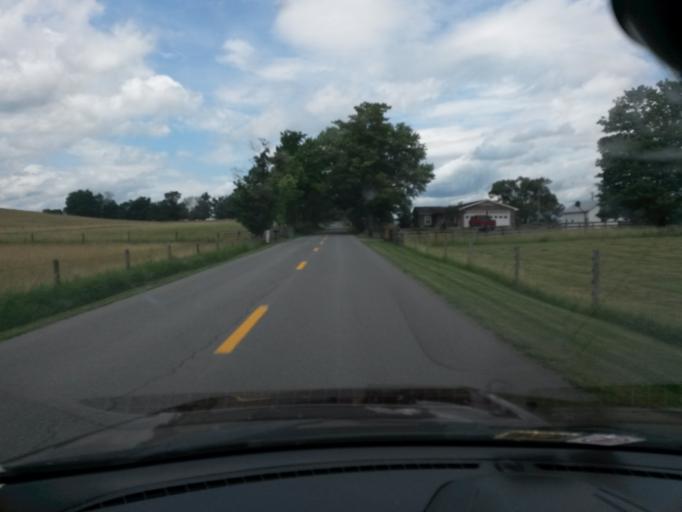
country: US
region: West Virginia
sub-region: Monroe County
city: Union
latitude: 37.5433
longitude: -80.5350
